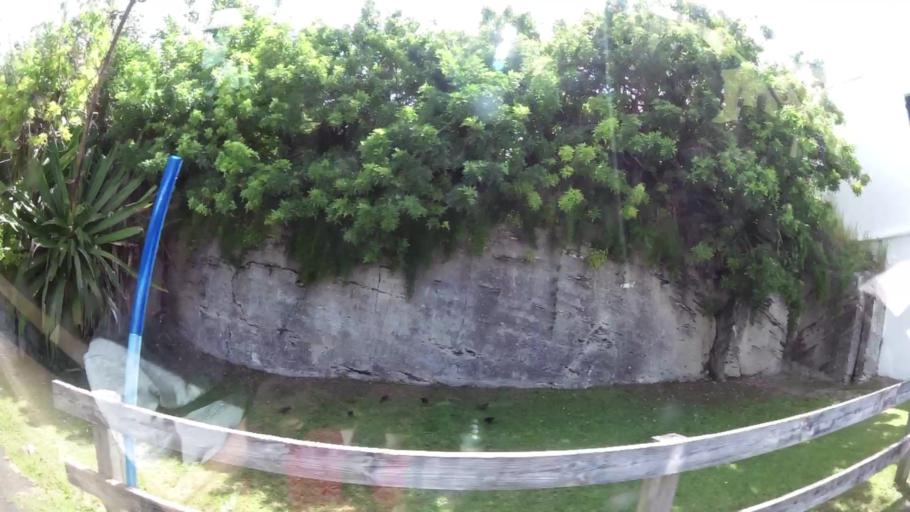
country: BM
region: Saint George
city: Saint George
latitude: 32.3659
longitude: -64.6531
